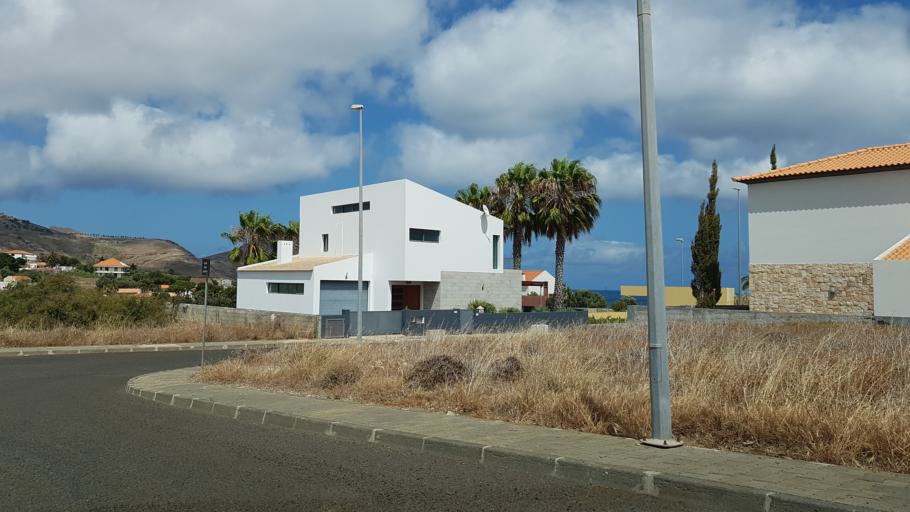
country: PT
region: Madeira
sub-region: Porto Santo
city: Vila de Porto Santo
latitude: 33.0570
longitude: -16.3420
